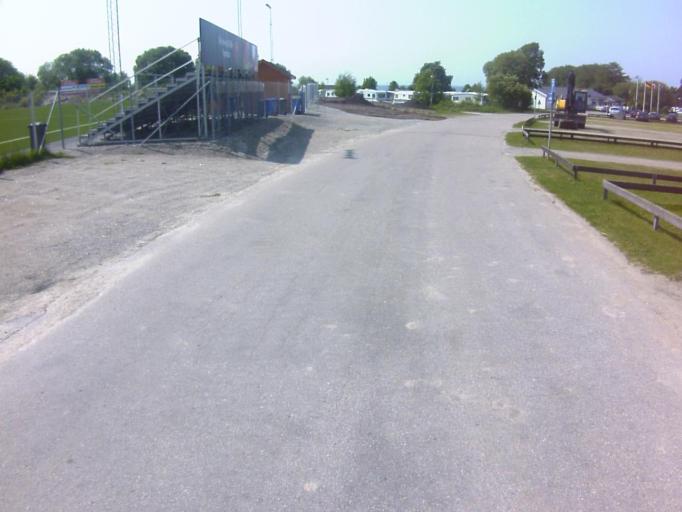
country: SE
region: Blekinge
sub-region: Solvesborgs Kommun
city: Soelvesborg
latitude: 56.0122
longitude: 14.7207
